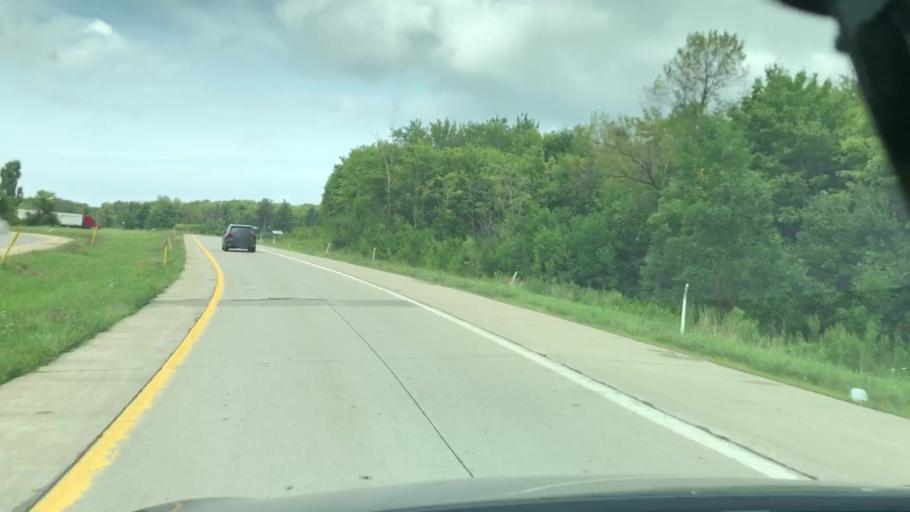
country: US
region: Pennsylvania
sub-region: Erie County
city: Erie
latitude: 42.0310
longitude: -80.1192
